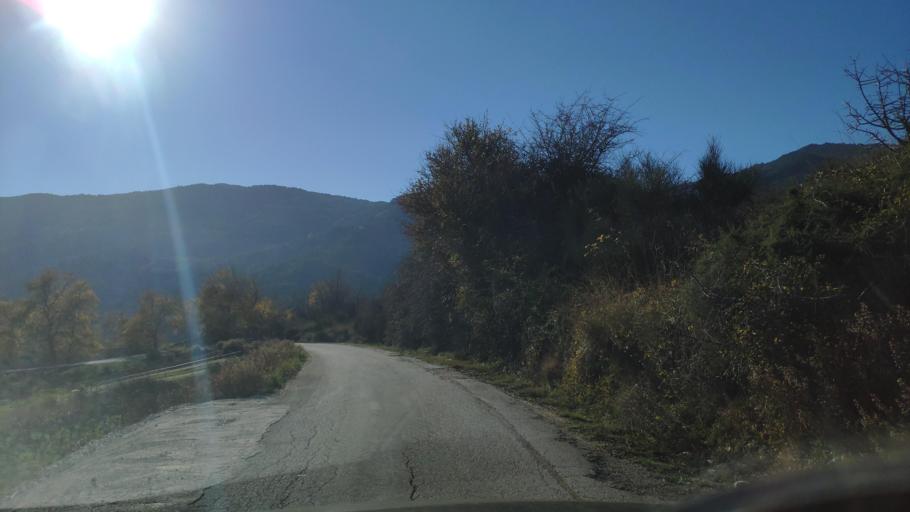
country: GR
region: Peloponnese
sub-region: Nomos Korinthias
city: Xylokastro
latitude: 38.0279
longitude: 22.4716
